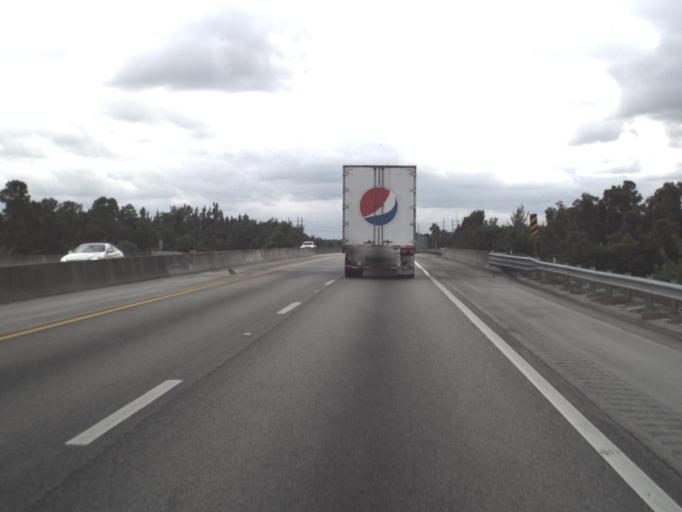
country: US
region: Florida
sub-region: Palm Beach County
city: Schall Circle
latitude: 26.7524
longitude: -80.1344
